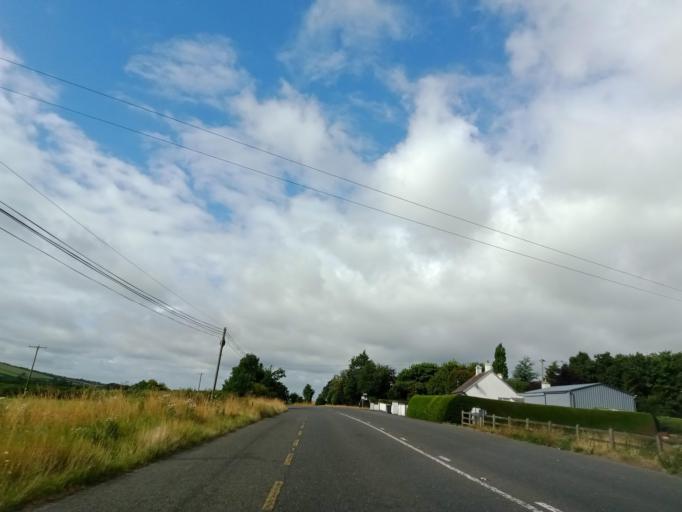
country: IE
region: Leinster
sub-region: Laois
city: Rathdowney
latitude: 52.8256
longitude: -7.4629
